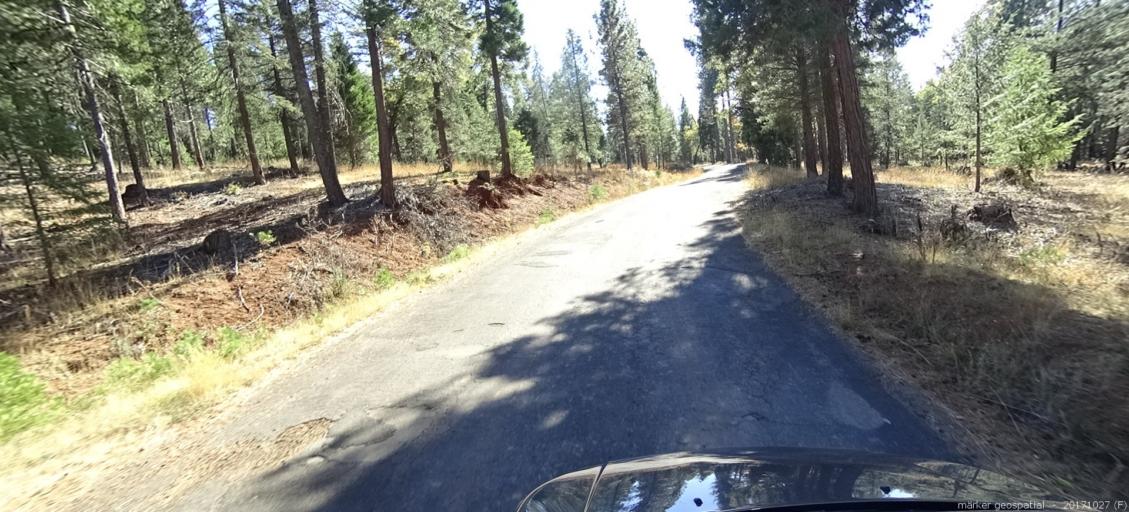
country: US
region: California
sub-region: Shasta County
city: Shingletown
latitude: 40.6178
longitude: -121.8368
